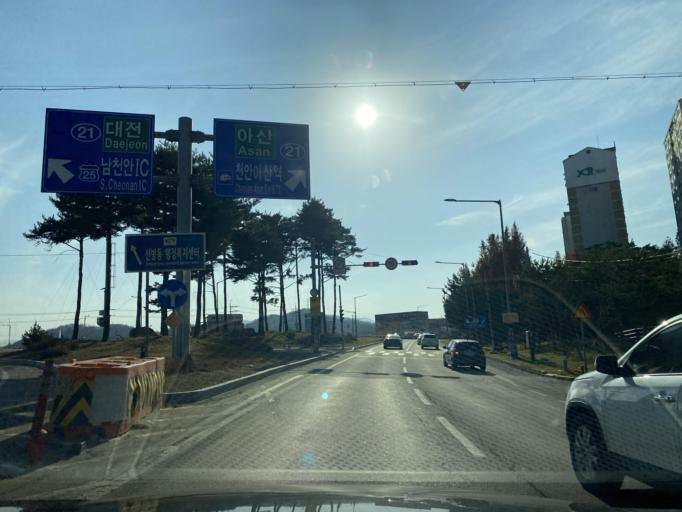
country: KR
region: Chungcheongnam-do
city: Cheonan
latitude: 36.7872
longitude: 127.1180
